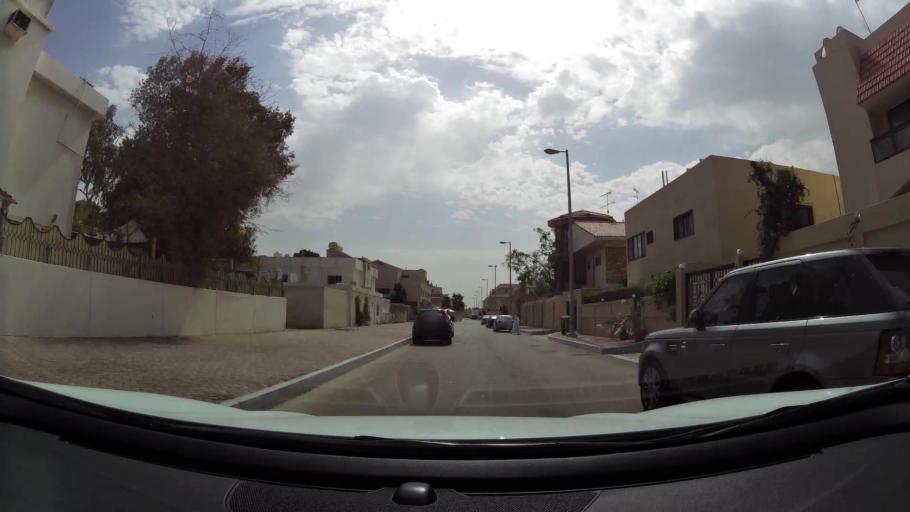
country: AE
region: Abu Dhabi
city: Abu Dhabi
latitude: 24.4547
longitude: 54.3554
